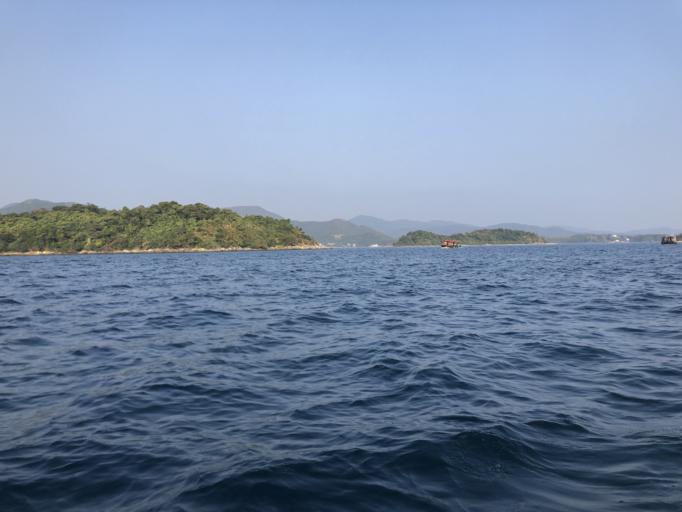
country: HK
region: Sai Kung
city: Sai Kung
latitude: 22.3771
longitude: 114.2792
